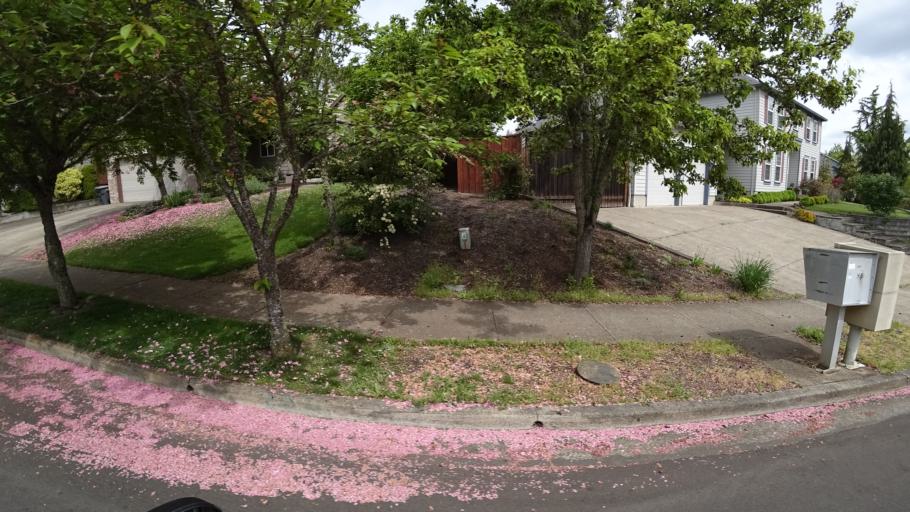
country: US
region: Oregon
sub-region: Washington County
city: Hillsboro
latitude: 45.5445
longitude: -122.9879
